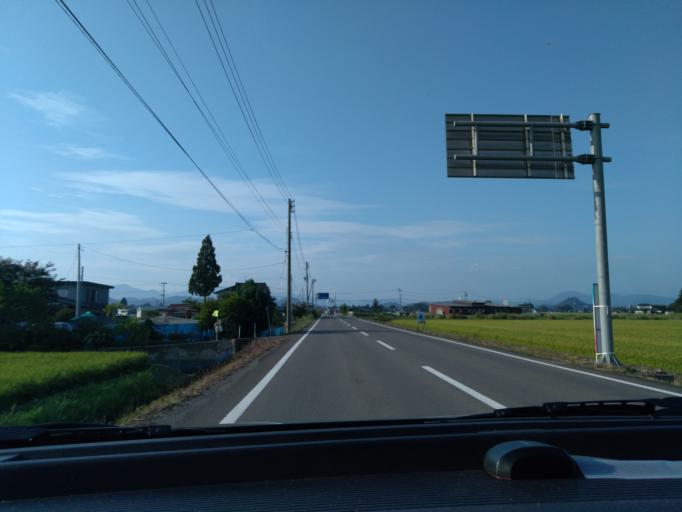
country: JP
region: Akita
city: Kakunodatemachi
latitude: 39.5468
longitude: 140.5577
